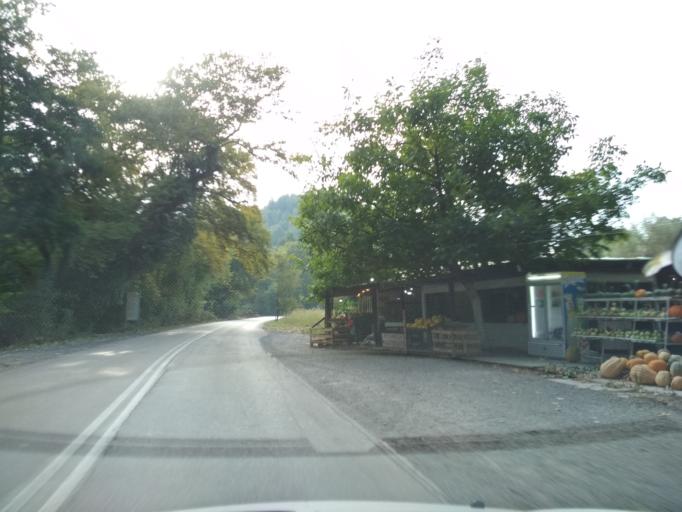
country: GR
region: Central Greece
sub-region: Nomos Evvoias
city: Mantoudi
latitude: 38.7765
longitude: 23.4720
